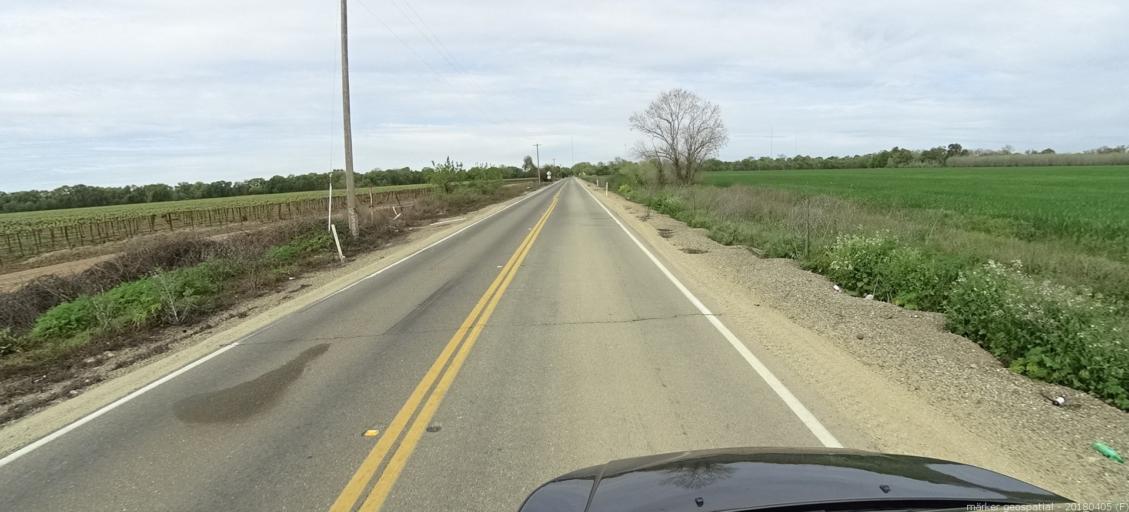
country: US
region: California
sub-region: San Joaquin County
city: Thornton
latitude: 38.2400
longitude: -121.4037
